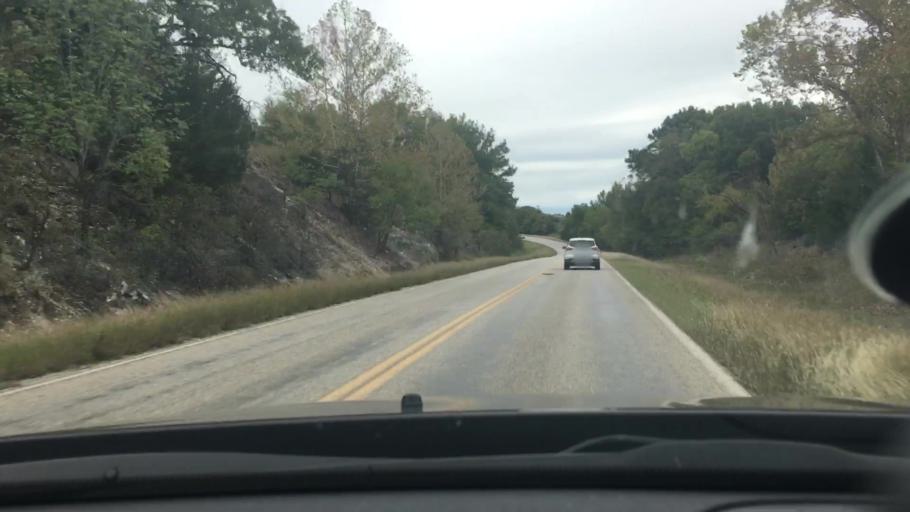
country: US
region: Oklahoma
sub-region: Johnston County
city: Tishomingo
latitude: 34.3316
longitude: -96.4195
